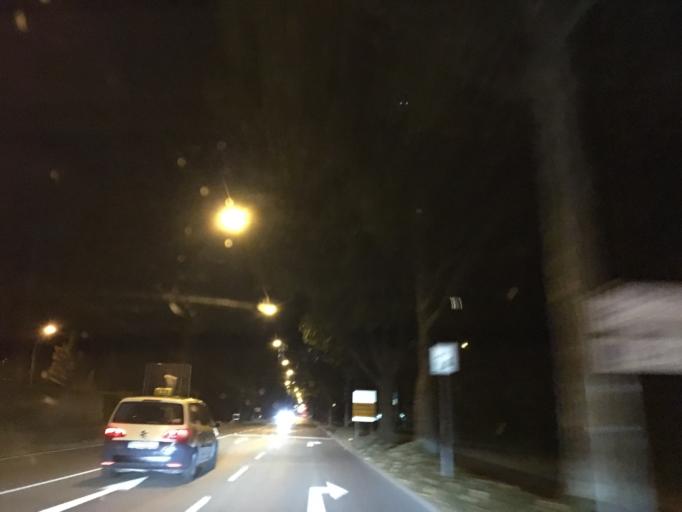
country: DE
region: Hesse
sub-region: Regierungsbezirk Darmstadt
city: Bad Soden am Taunus
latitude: 50.1346
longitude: 8.5118
